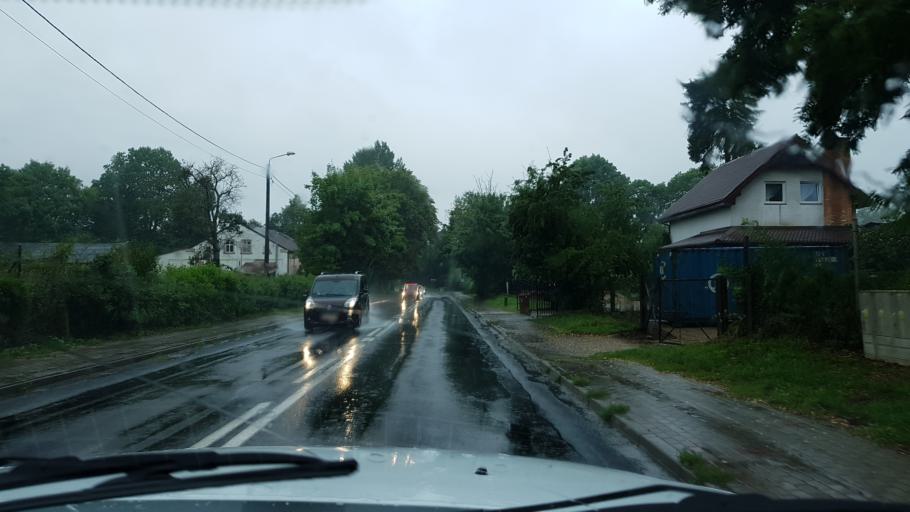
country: PL
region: West Pomeranian Voivodeship
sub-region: Powiat kolobrzeski
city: Grzybowo
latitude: 54.1043
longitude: 15.5169
